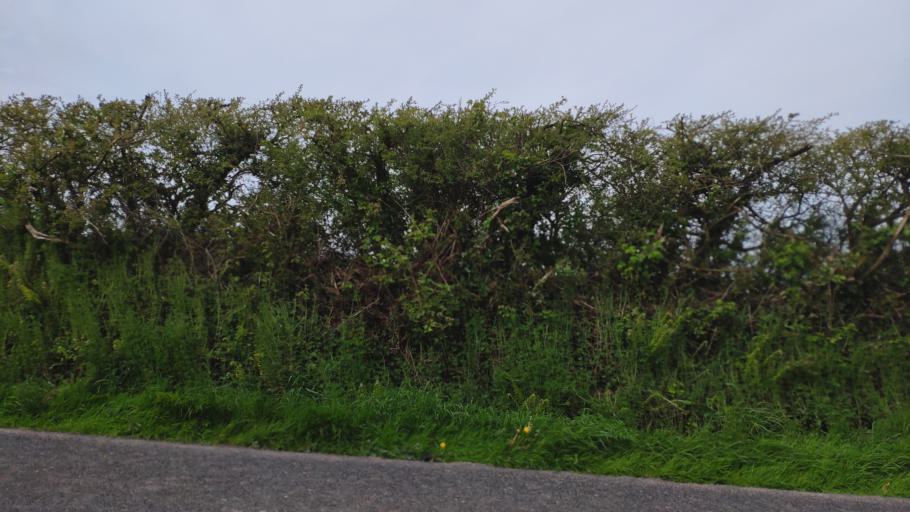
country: IE
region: Munster
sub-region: County Cork
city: Cork
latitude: 51.9669
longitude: -8.4695
